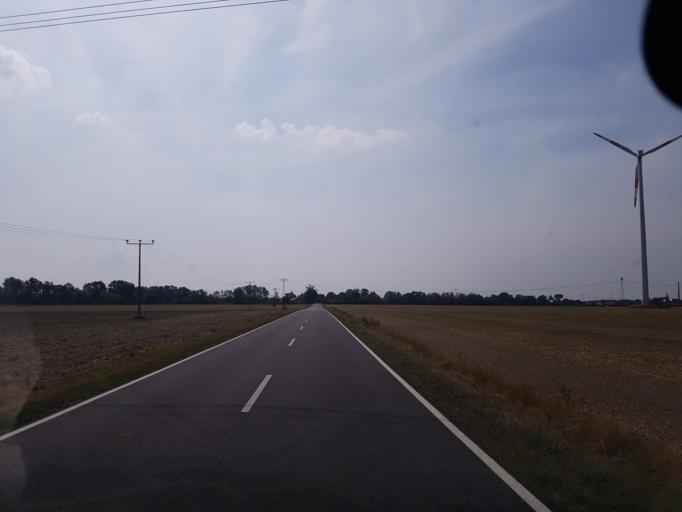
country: DE
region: Brandenburg
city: Finsterwalde
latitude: 51.6524
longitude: 13.7350
